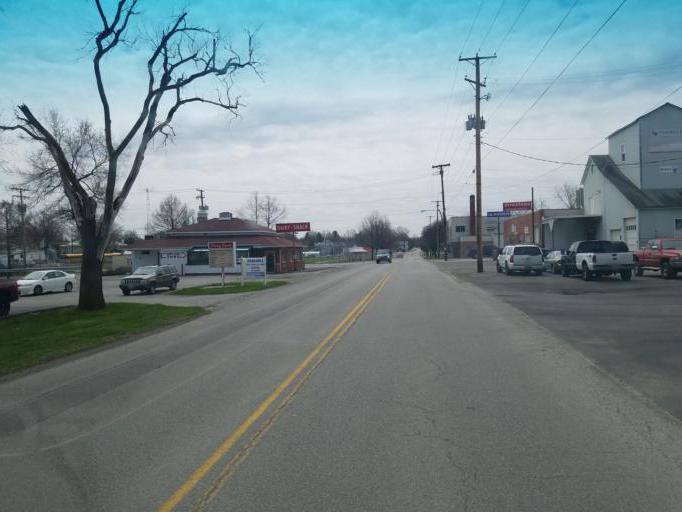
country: US
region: Ohio
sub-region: Wyandot County
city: Upper Sandusky
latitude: 40.8310
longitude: -83.2901
